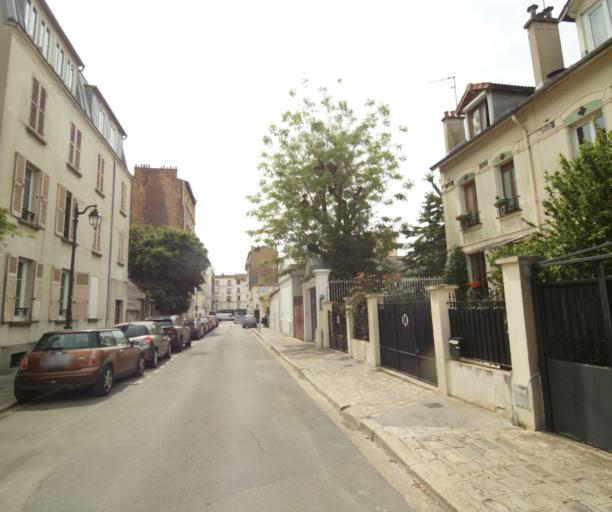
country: FR
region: Ile-de-France
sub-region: Departement des Hauts-de-Seine
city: Asnieres-sur-Seine
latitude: 48.9159
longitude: 2.2843
